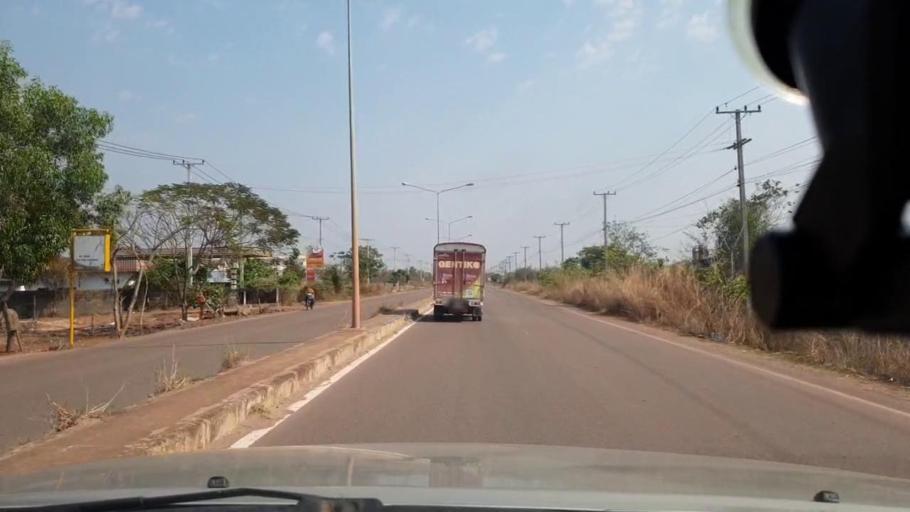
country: LA
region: Vientiane
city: Vientiane
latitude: 18.0136
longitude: 102.7231
